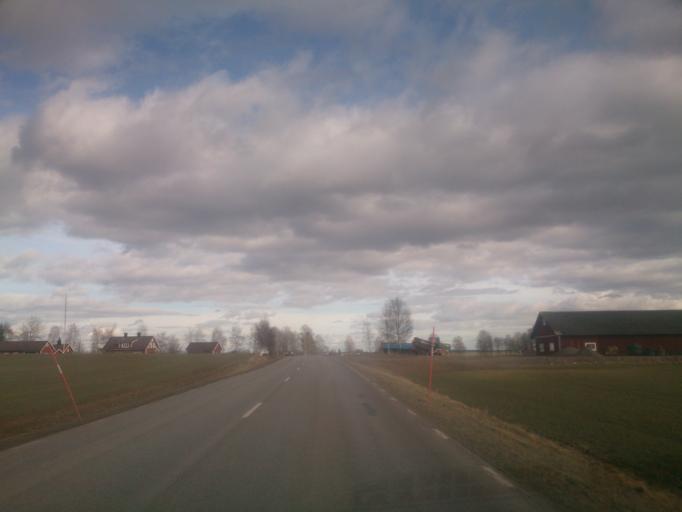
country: SE
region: OEstergoetland
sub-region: Motala Kommun
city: Stenstorp
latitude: 58.5200
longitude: 15.1408
